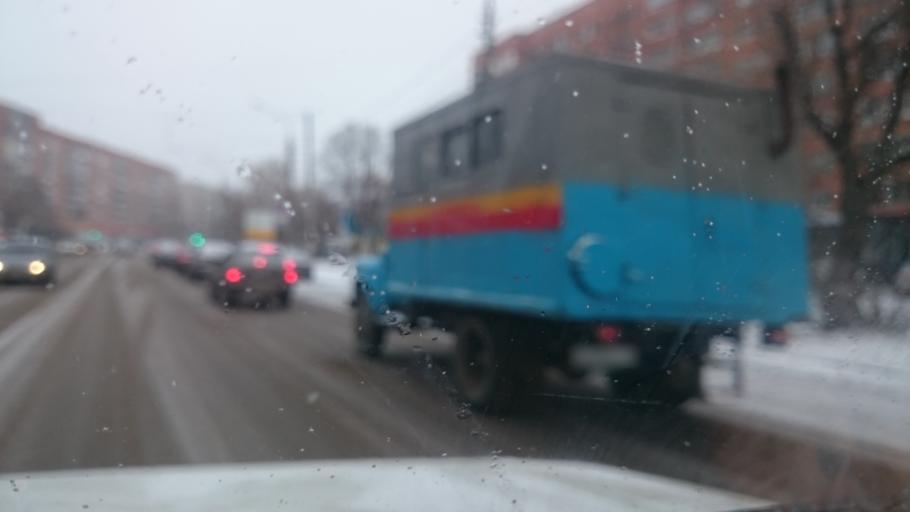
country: RU
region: Tula
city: Tula
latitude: 54.1956
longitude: 37.6014
